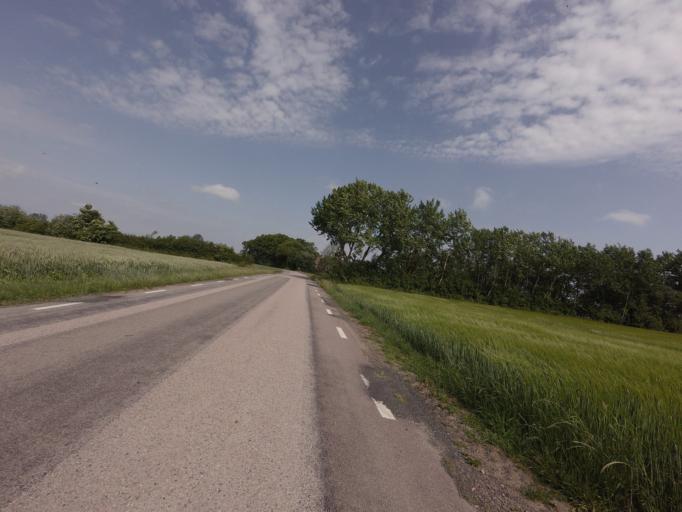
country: SE
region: Skane
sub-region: Hoganas Kommun
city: Hoganas
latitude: 56.1848
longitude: 12.6585
